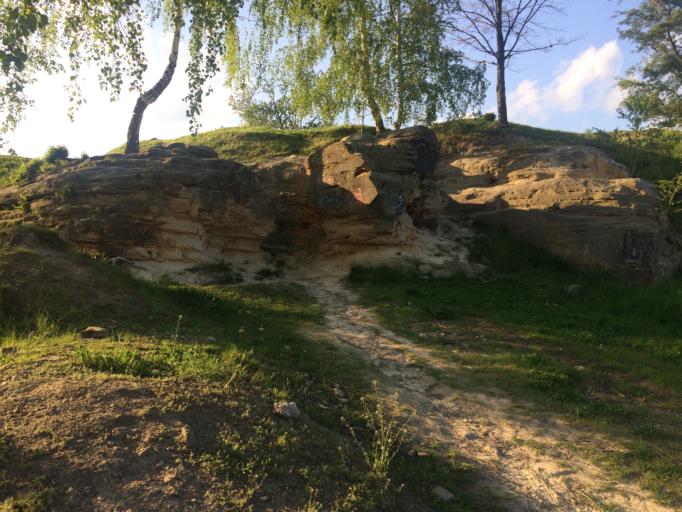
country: PL
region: Swietokrzyskie
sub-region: Powiat starachowicki
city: Starachowice
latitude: 51.0498
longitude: 21.0820
